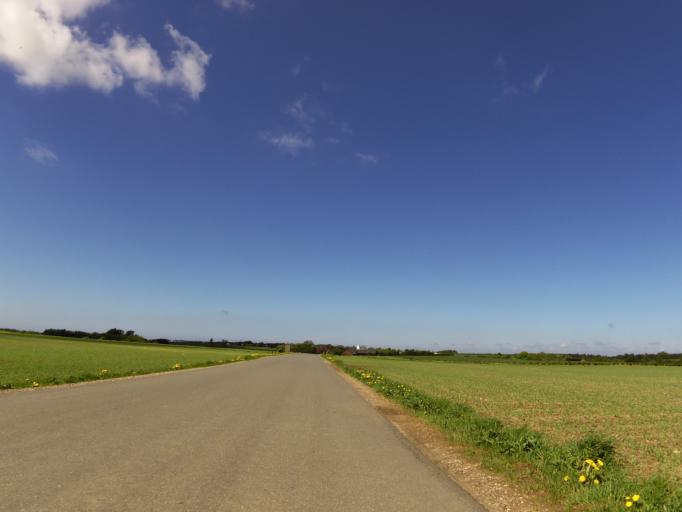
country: DK
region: Central Jutland
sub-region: Holstebro Kommune
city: Vinderup
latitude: 56.4213
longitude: 8.7846
